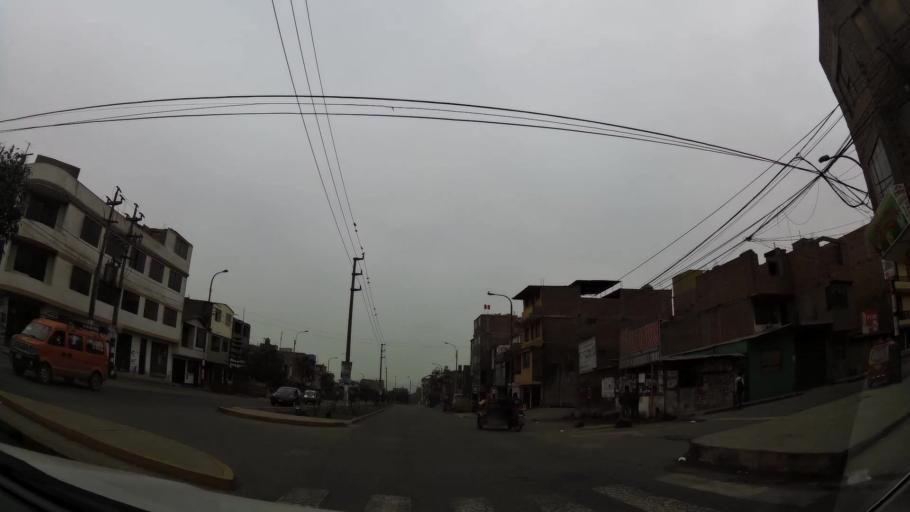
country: PE
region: Lima
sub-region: Lima
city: Independencia
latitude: -11.9581
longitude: -76.9837
